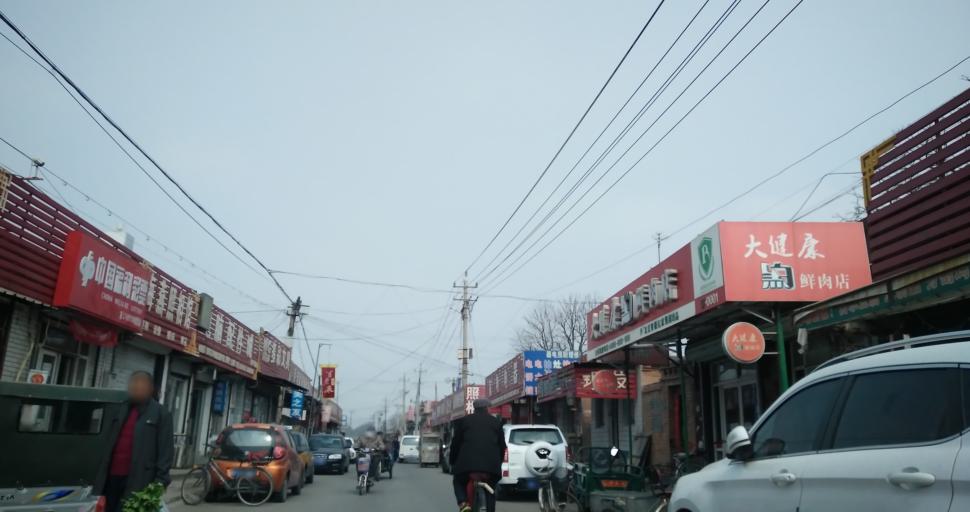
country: CN
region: Beijing
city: Qingyundian
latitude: 39.6786
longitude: 116.5080
